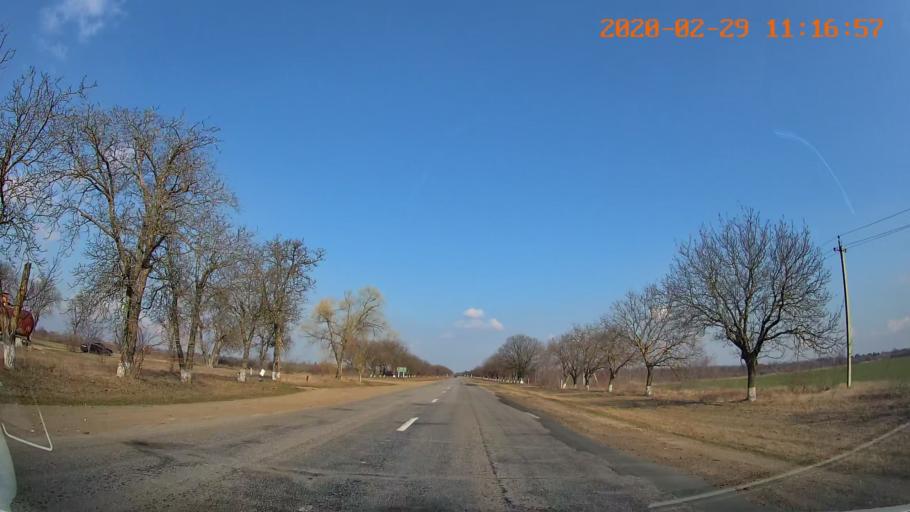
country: MD
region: Telenesti
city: Dubasari
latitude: 47.3157
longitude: 29.1692
